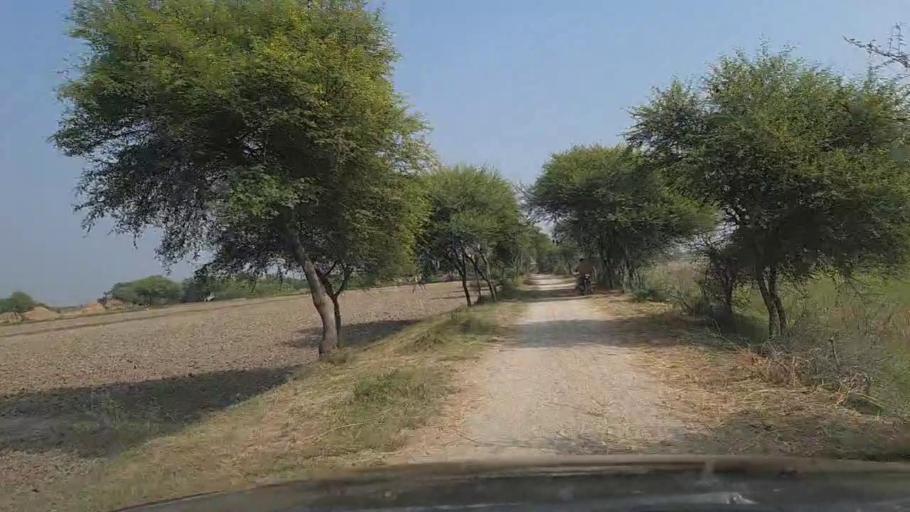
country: PK
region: Sindh
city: Mirpur Batoro
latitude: 24.6963
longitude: 68.2450
